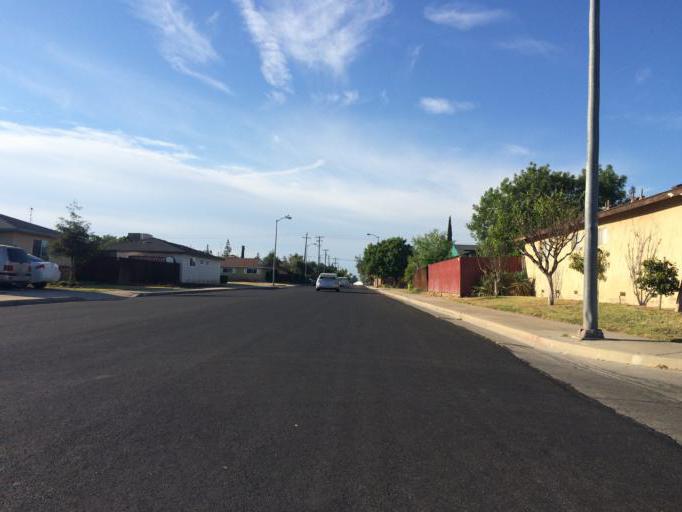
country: US
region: California
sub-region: Fresno County
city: Tarpey Village
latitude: 36.7997
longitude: -119.7137
